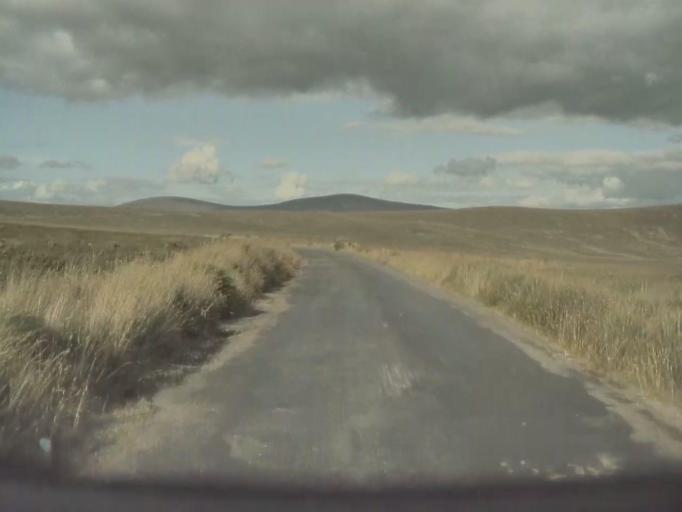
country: IE
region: Leinster
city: Oldbawn
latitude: 53.1048
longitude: -6.3284
